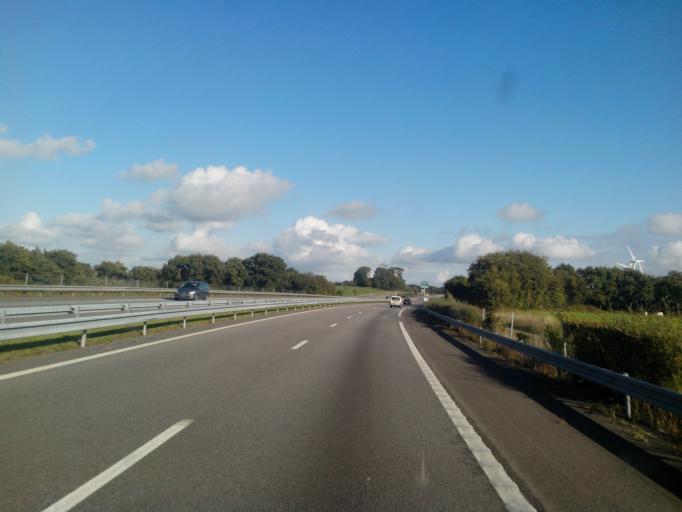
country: FR
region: Brittany
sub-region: Departement du Morbihan
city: Ambon
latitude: 47.5923
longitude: -2.5580
